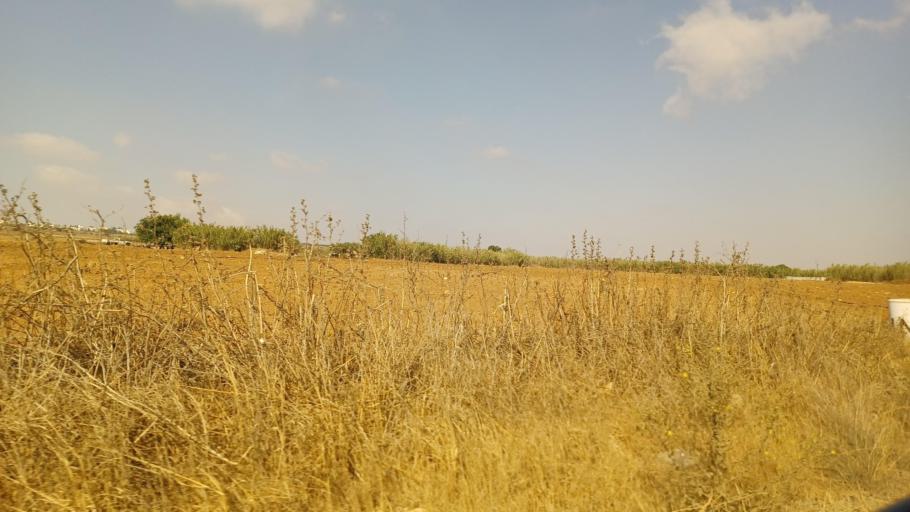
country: CY
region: Ammochostos
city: Paralimni
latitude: 35.0682
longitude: 33.9984
